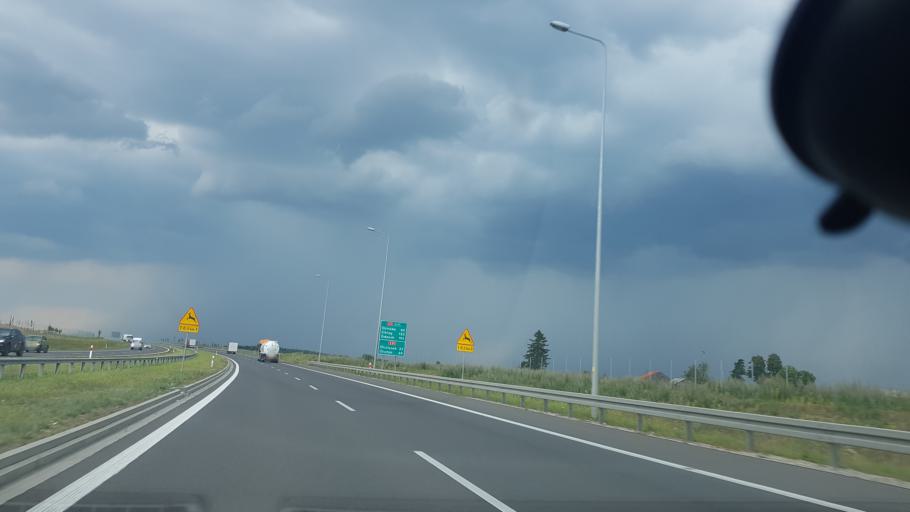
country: PL
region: Warmian-Masurian Voivodeship
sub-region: Powiat nidzicki
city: Nidzica
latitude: 53.3349
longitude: 20.4344
